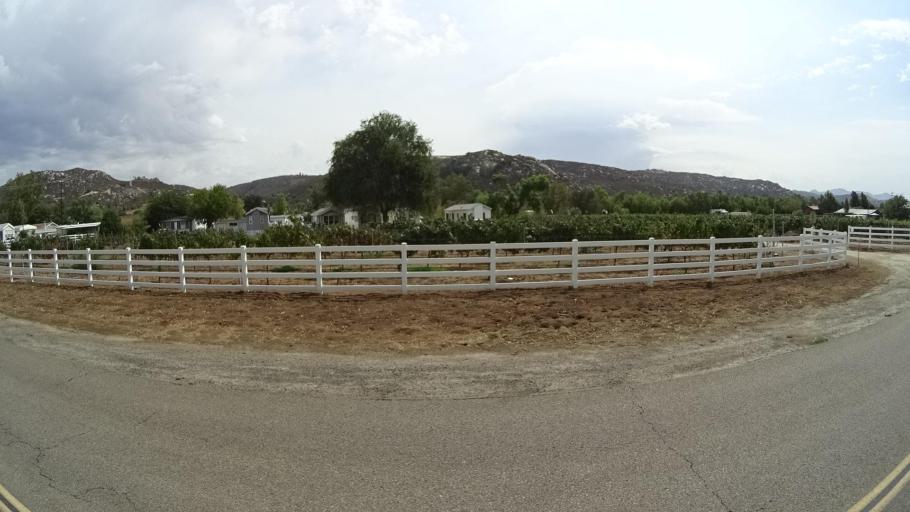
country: US
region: California
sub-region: San Diego County
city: Ramona
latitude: 33.0774
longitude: -116.8418
